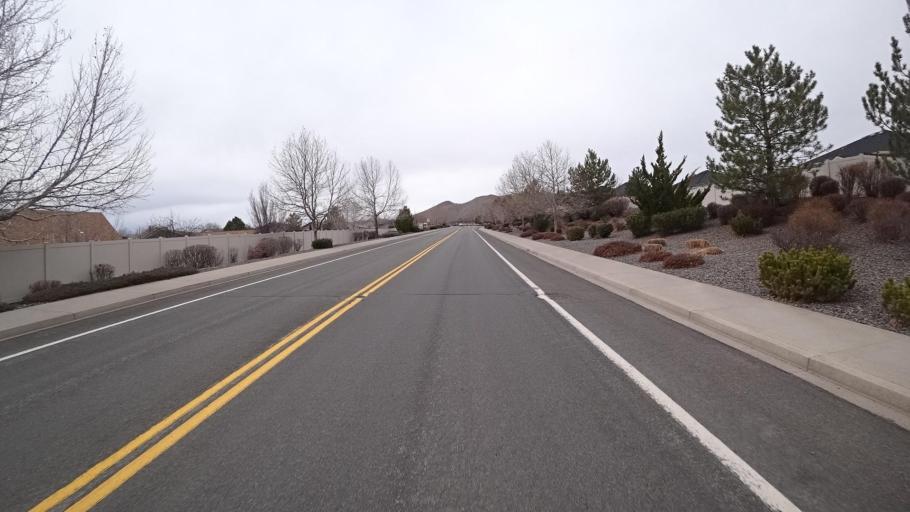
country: US
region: Nevada
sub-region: Washoe County
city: Spanish Springs
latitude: 39.6572
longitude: -119.7299
